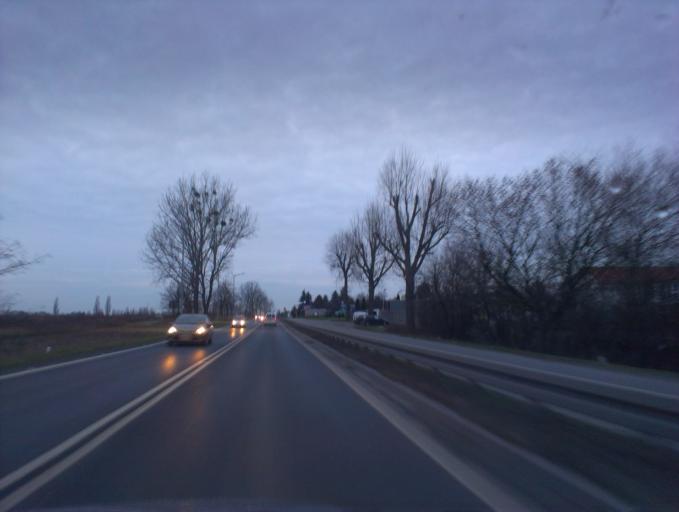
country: PL
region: Greater Poland Voivodeship
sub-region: Powiat poznanski
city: Zlotniki
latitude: 52.4883
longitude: 16.8512
